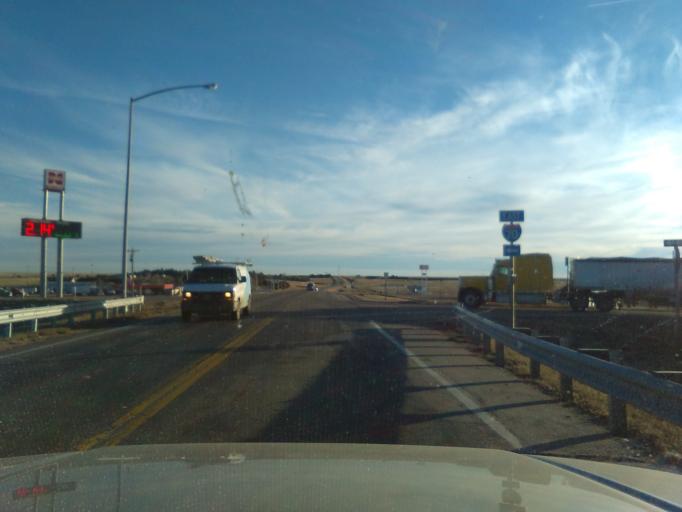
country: US
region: Kansas
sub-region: Logan County
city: Oakley
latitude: 39.1887
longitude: -100.8700
